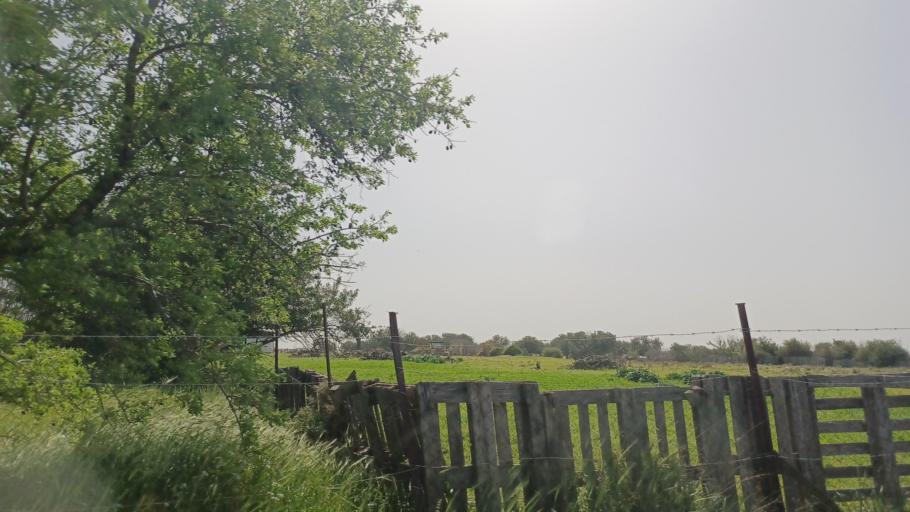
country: CY
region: Limassol
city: Pissouri
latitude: 34.7267
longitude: 32.7285
